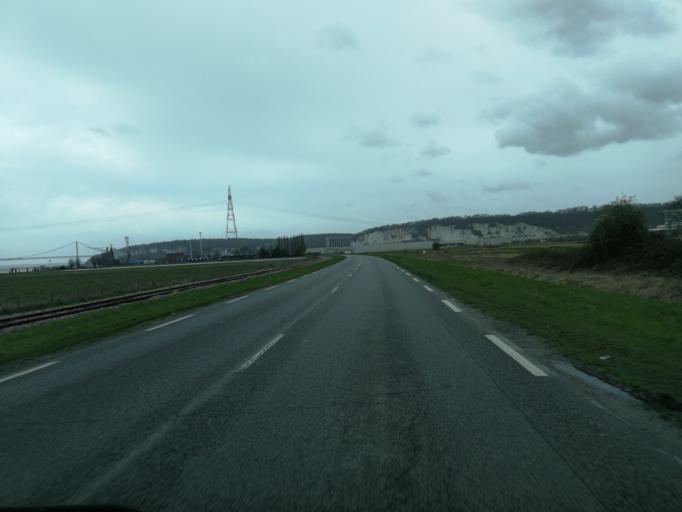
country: FR
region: Haute-Normandie
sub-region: Departement de la Seine-Maritime
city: Saint-Nicolas-de-la-Taille
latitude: 49.4895
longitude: 0.4978
